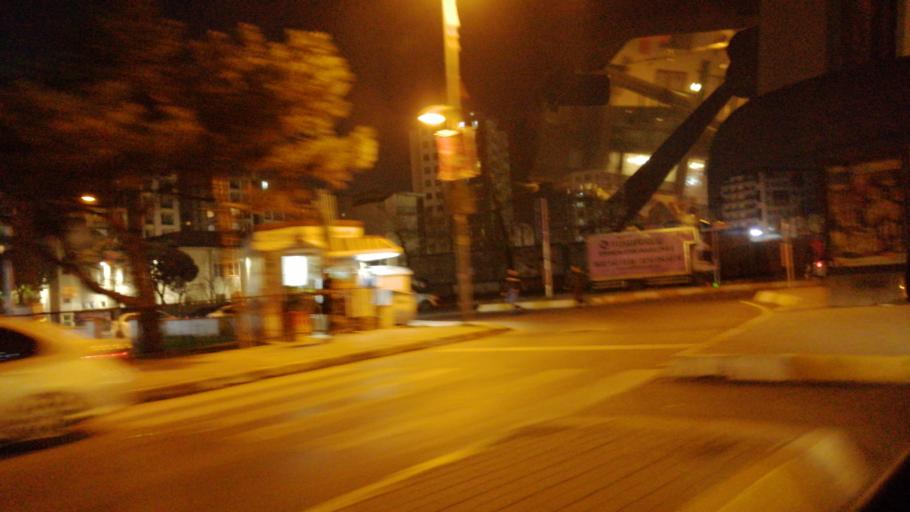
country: TR
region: Istanbul
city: Umraniye
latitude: 41.0156
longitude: 29.1287
